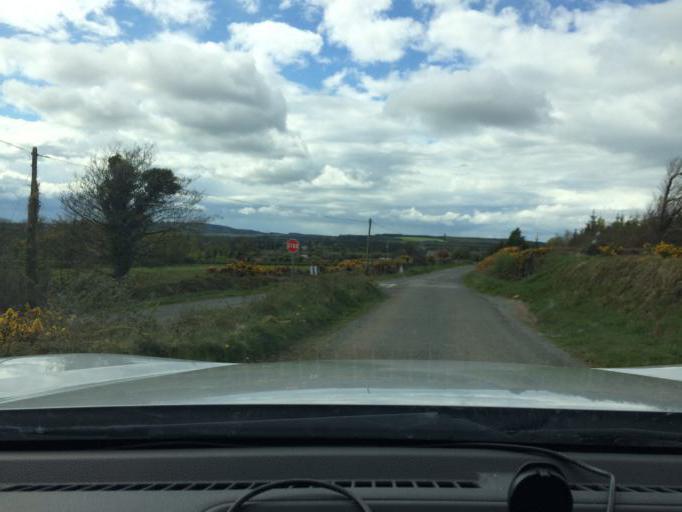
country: IE
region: Munster
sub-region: Waterford
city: Dungarvan
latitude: 52.0418
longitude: -7.6453
